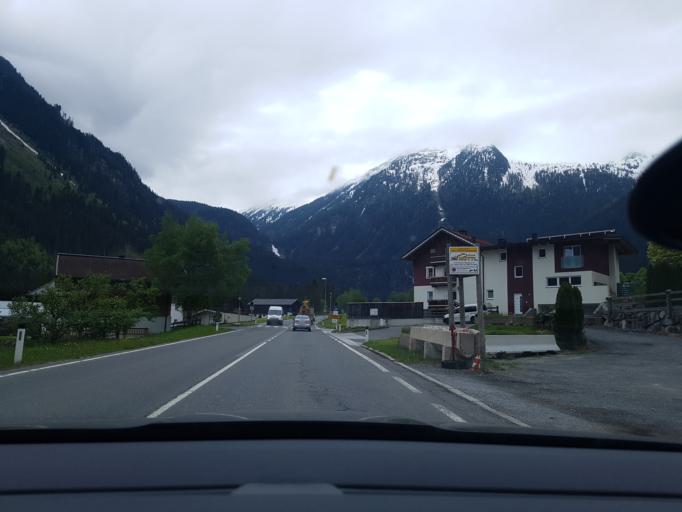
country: AT
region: Salzburg
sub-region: Politischer Bezirk Zell am See
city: Krimml
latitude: 47.2212
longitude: 12.1773
